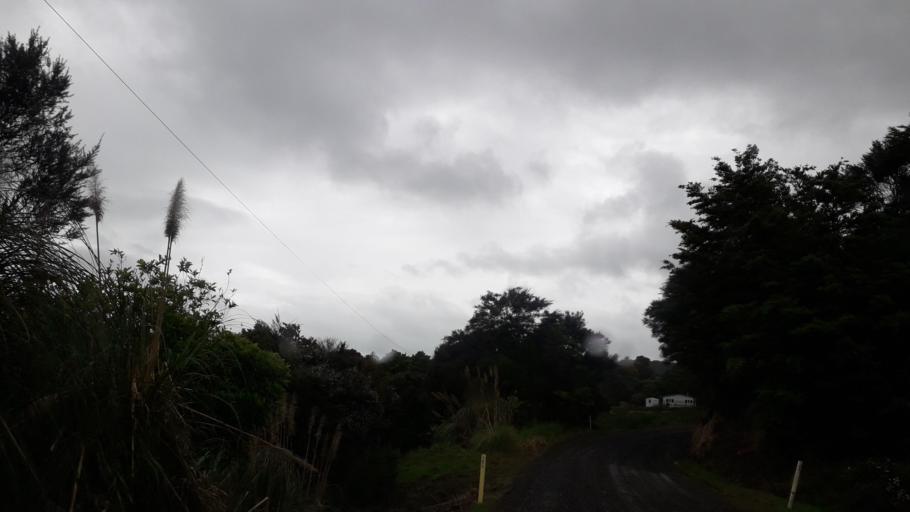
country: NZ
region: Northland
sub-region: Far North District
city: Kaitaia
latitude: -35.3859
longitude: 173.4063
